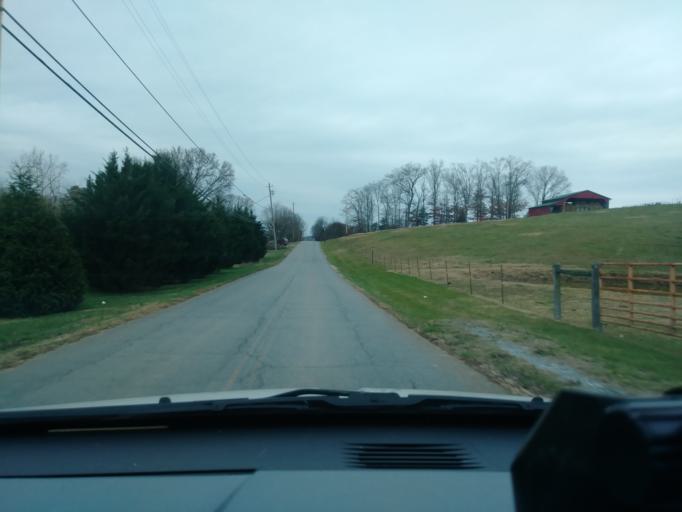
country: US
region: Tennessee
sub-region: Greene County
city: Greeneville
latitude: 36.1075
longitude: -82.8854
